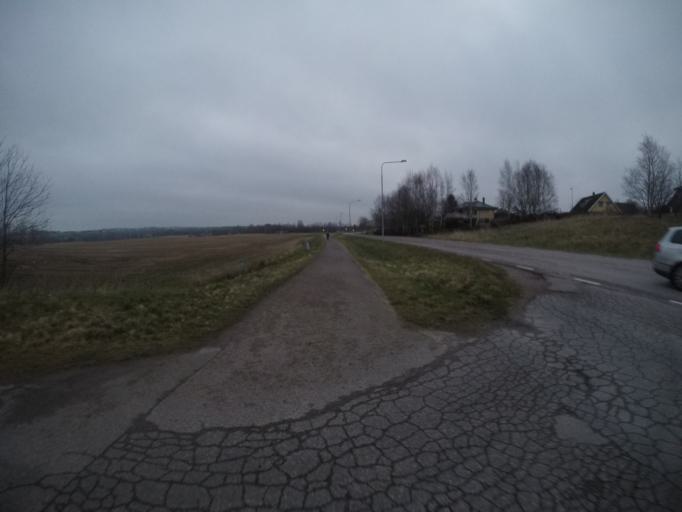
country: SE
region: Halland
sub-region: Laholms Kommun
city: Laholm
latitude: 56.5039
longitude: 13.0136
